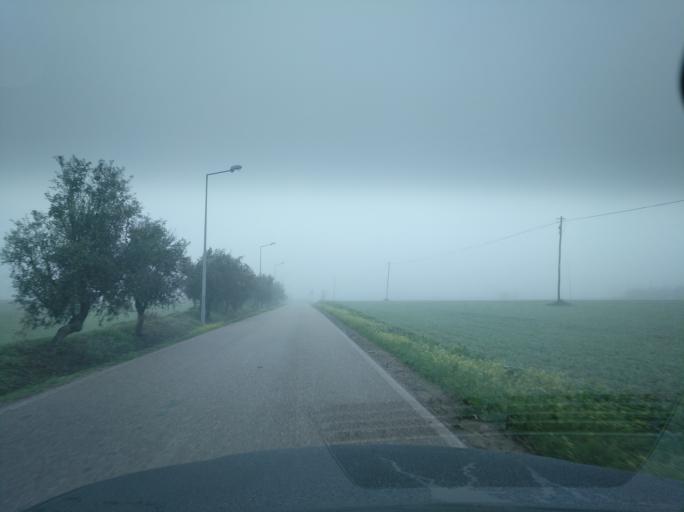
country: PT
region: Portalegre
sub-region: Campo Maior
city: Campo Maior
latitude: 39.0234
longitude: -7.0680
